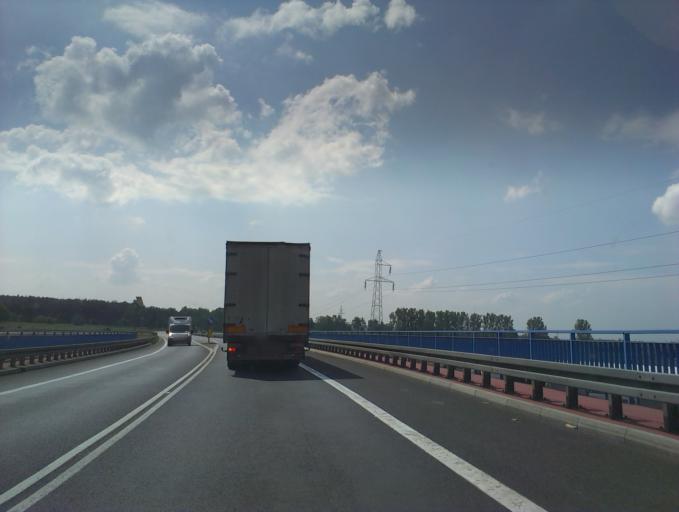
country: PL
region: Greater Poland Voivodeship
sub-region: Powiat pilski
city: Pila
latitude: 53.1421
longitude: 16.7841
